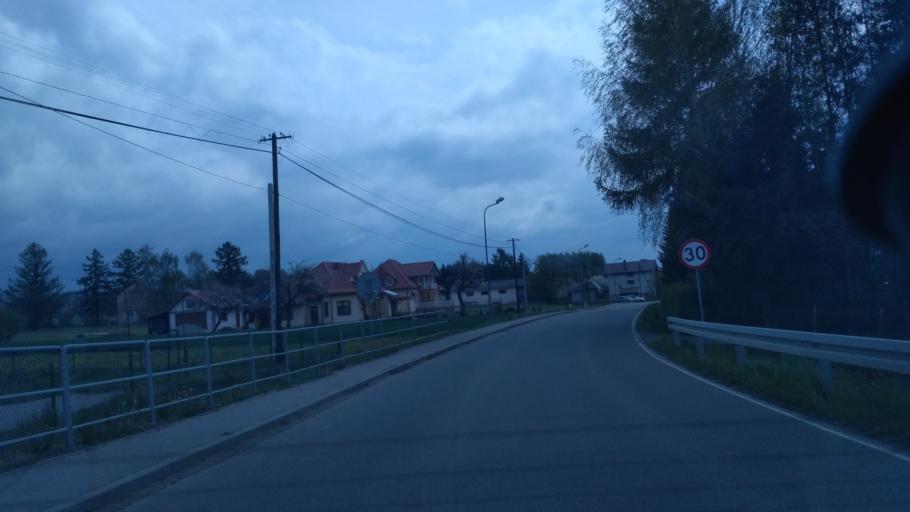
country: PL
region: Subcarpathian Voivodeship
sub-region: Powiat brzozowski
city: Haczow
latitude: 49.6644
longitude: 21.9033
